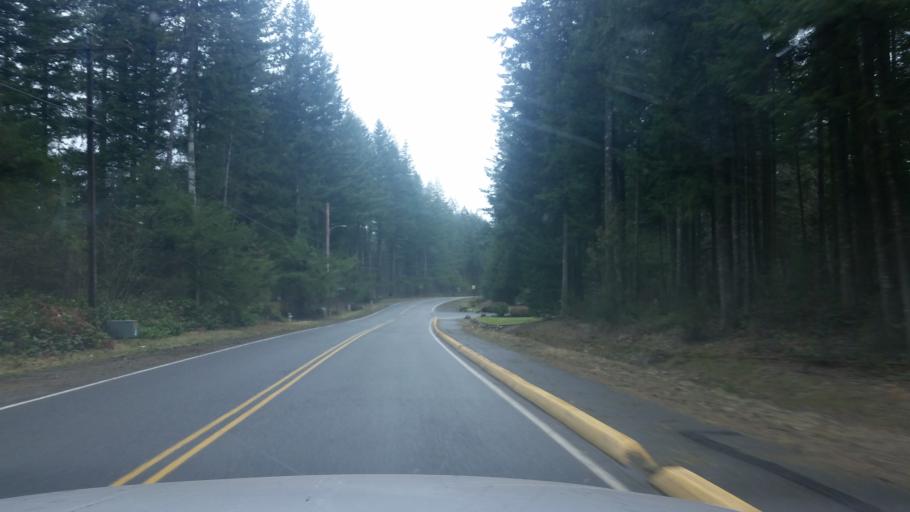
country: US
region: Washington
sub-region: King County
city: Tanner
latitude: 47.4724
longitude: -121.7222
